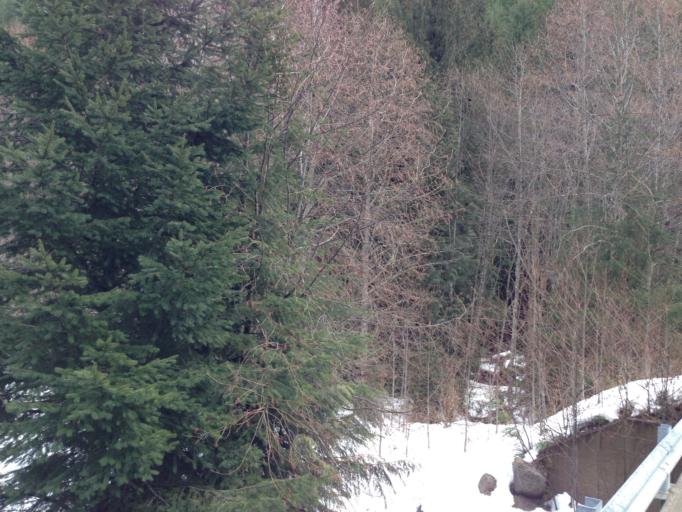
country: CA
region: British Columbia
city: Hope
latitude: 49.0462
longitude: -121.3980
